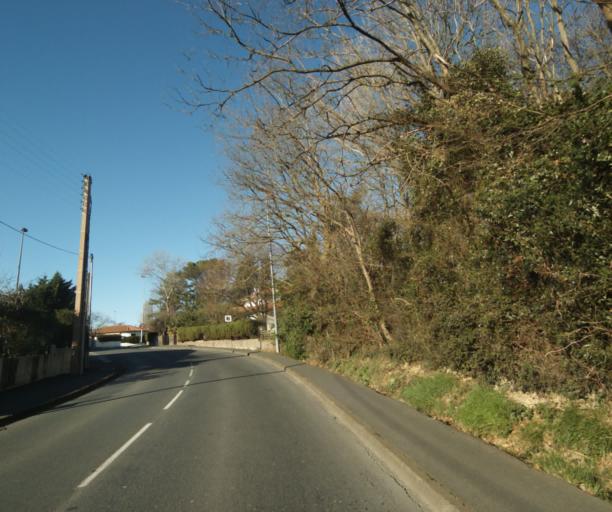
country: FR
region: Aquitaine
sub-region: Departement des Pyrenees-Atlantiques
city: Hendaye
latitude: 43.3681
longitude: -1.7560
